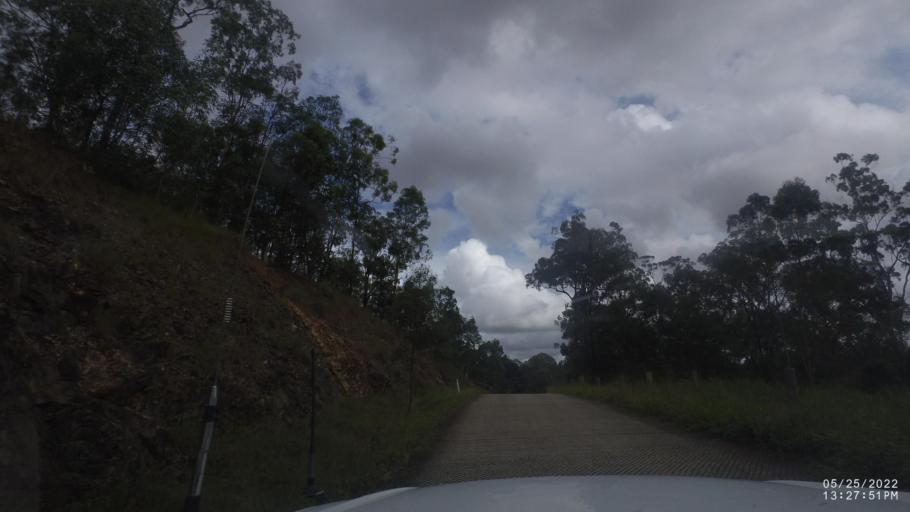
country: AU
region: Queensland
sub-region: Logan
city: Windaroo
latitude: -27.7938
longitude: 153.1502
